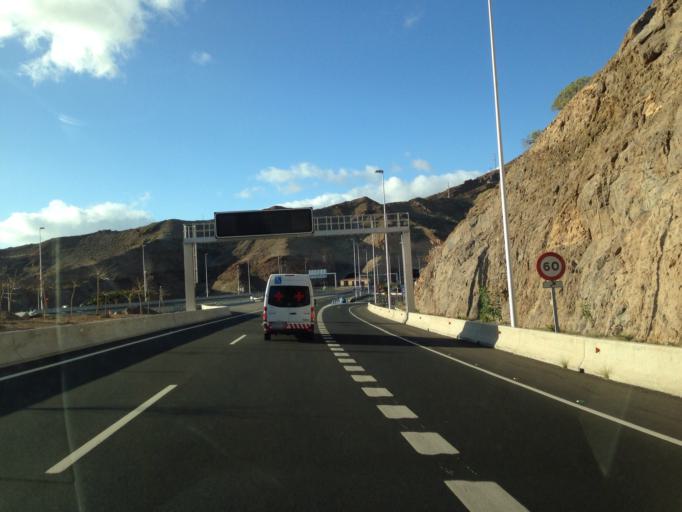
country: ES
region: Canary Islands
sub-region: Provincia de Las Palmas
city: Puerto Rico
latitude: 27.8005
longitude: -15.7053
